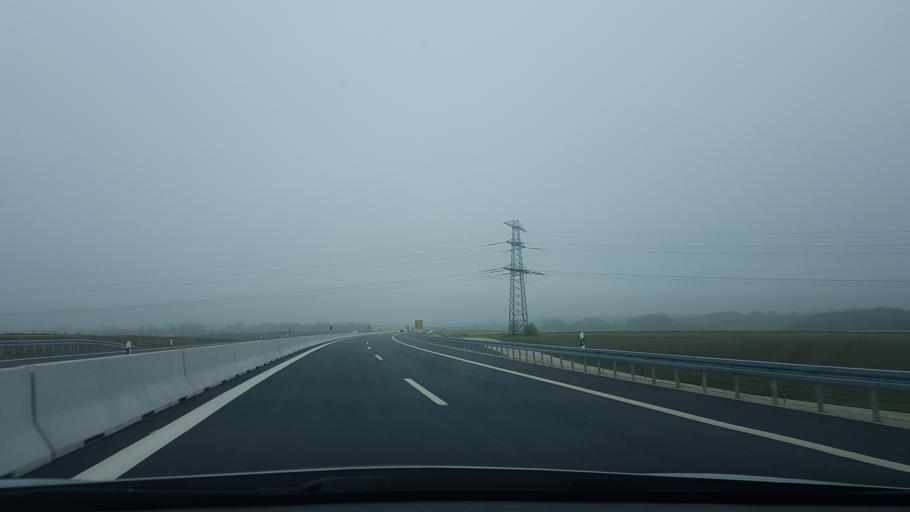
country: DE
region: Bavaria
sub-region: Lower Bavaria
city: Buch
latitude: 48.6591
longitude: 12.1872
